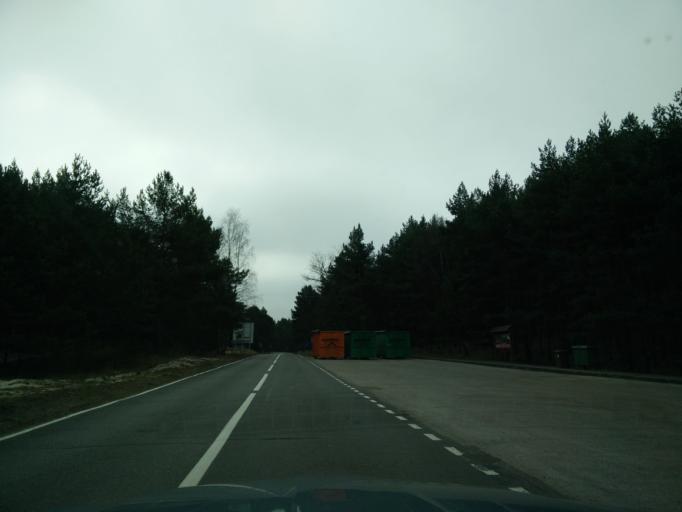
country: LT
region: Klaipedos apskritis
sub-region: Klaipeda
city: Klaipeda
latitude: 55.6784
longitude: 21.1131
